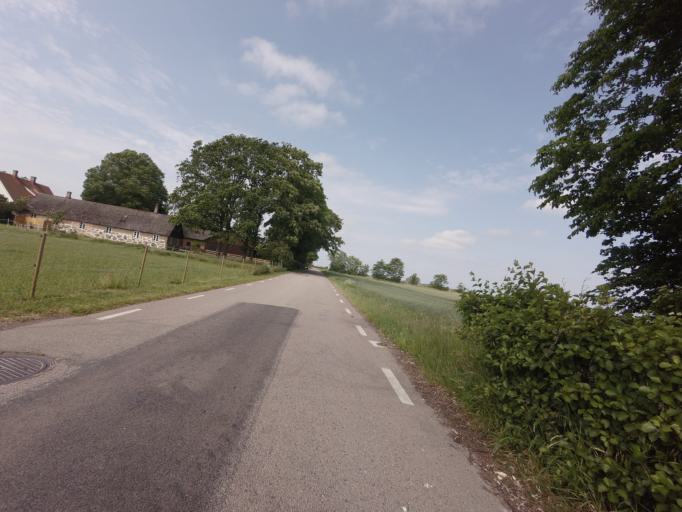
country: SE
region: Skane
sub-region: Hoganas Kommun
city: Hoganas
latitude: 56.1880
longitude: 12.6389
